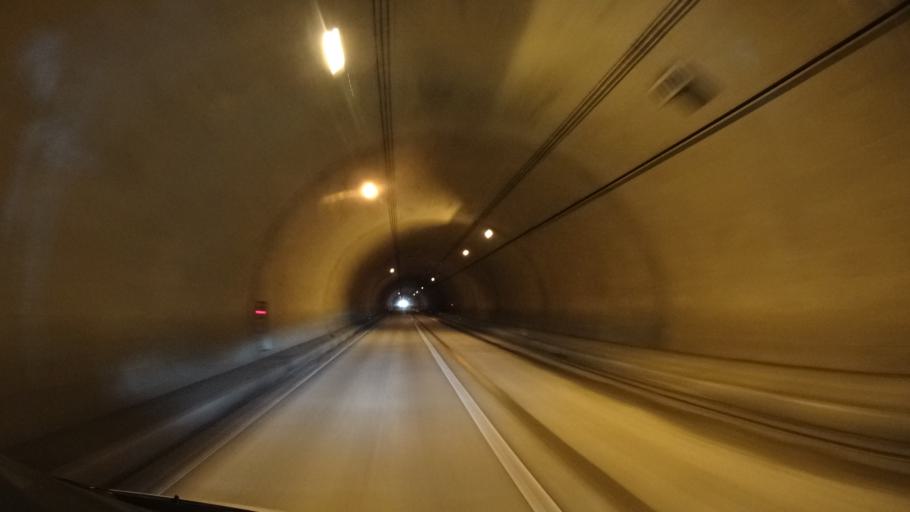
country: JP
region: Kyoto
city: Miyazu
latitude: 35.6779
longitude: 135.2782
